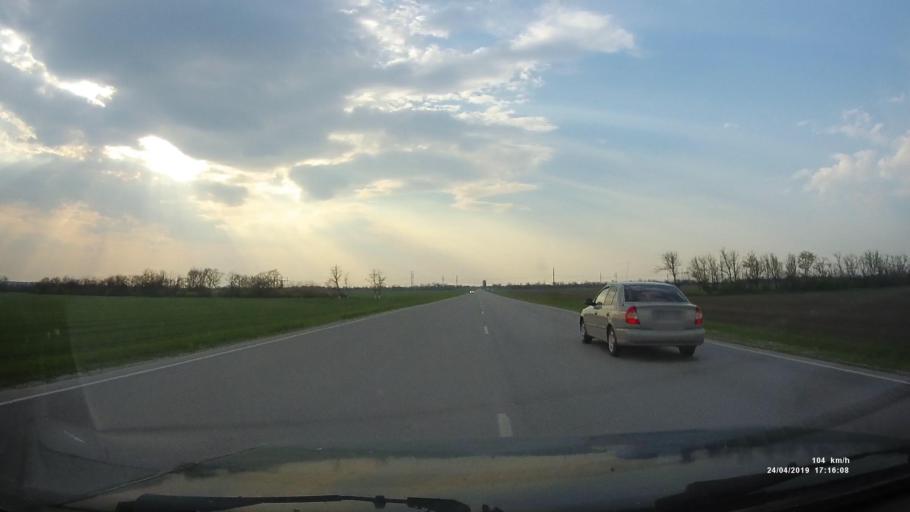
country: RU
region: Rostov
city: Gigant
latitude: 46.4958
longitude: 41.4313
